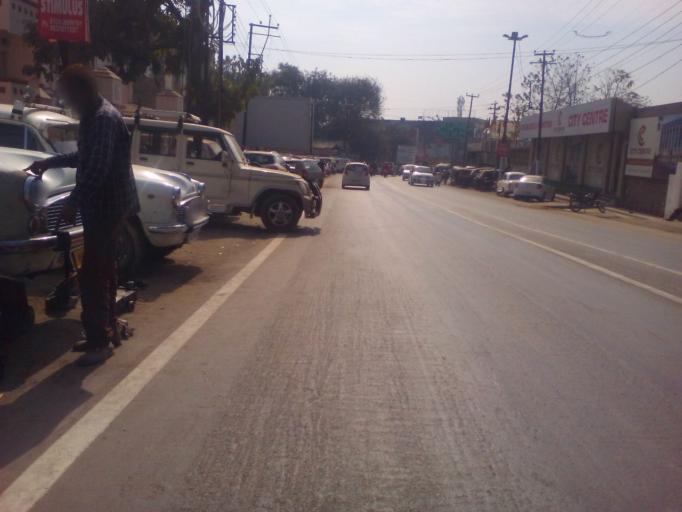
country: IN
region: Uttarakhand
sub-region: Dehradun
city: Dehradun
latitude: 30.3184
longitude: 78.0398
